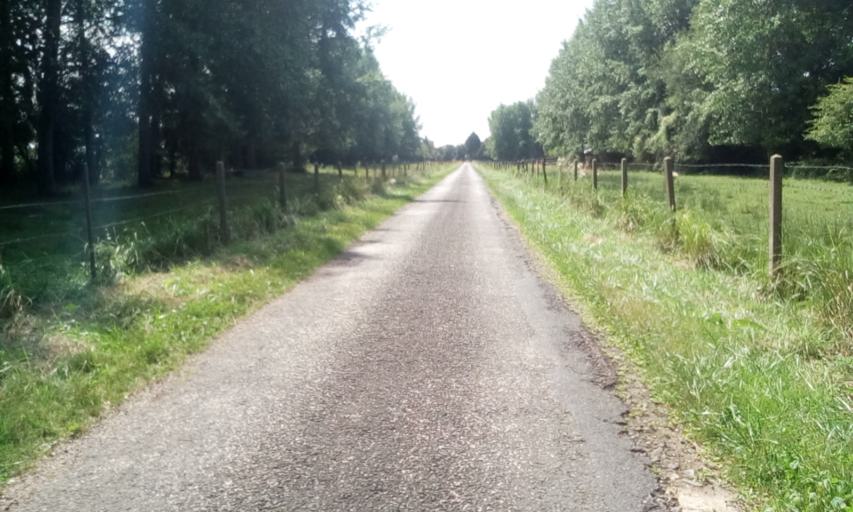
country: FR
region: Lower Normandy
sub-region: Departement du Calvados
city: Bellengreville
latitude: 49.1374
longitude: -0.2228
